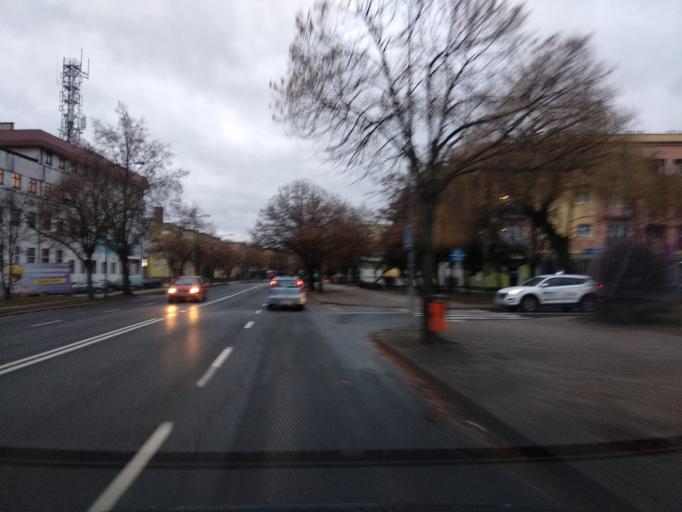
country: PL
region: Greater Poland Voivodeship
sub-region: Konin
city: Konin
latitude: 52.2281
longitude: 18.2591
